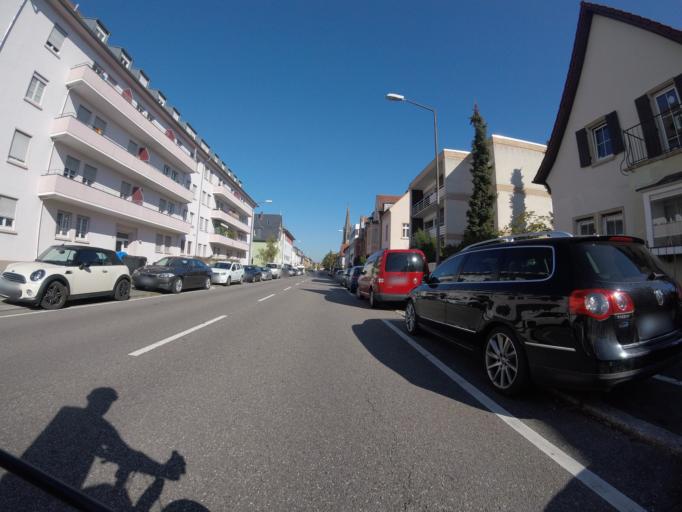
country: DE
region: Rheinland-Pfalz
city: Speyer
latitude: 49.3120
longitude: 8.4270
